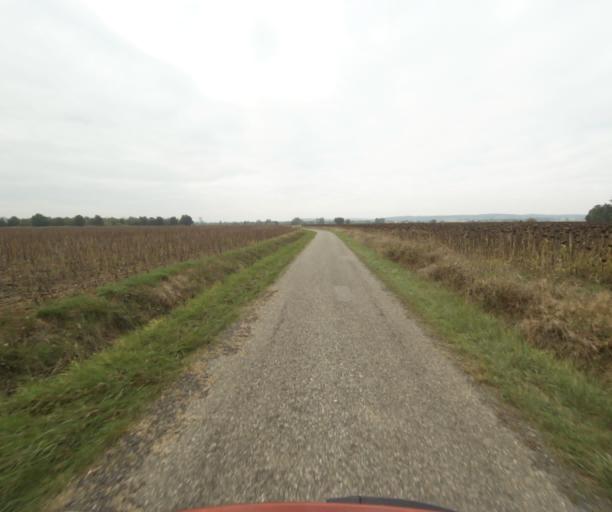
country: FR
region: Midi-Pyrenees
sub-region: Departement de la Haute-Garonne
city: Launac
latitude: 43.8073
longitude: 1.1844
